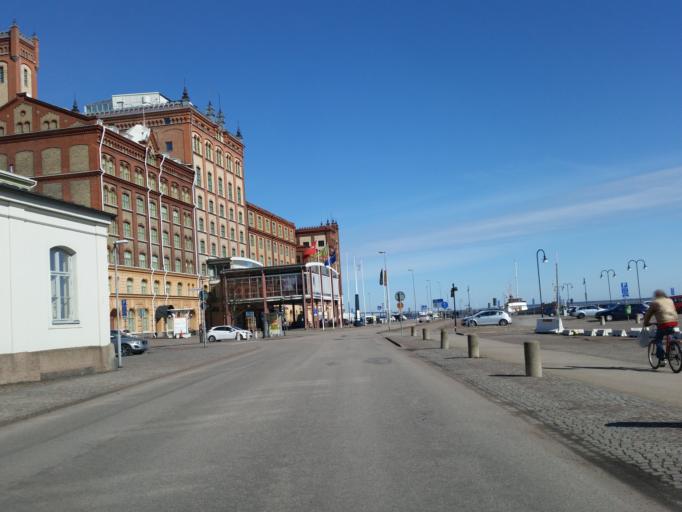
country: SE
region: Kalmar
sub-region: Kalmar Kommun
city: Kalmar
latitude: 56.6632
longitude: 16.3689
